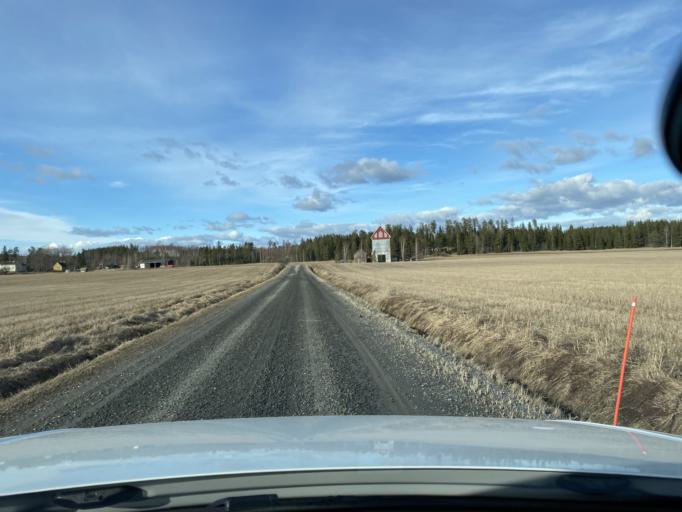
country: FI
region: Pirkanmaa
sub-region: Lounais-Pirkanmaa
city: Punkalaidun
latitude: 61.1342
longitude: 23.2074
